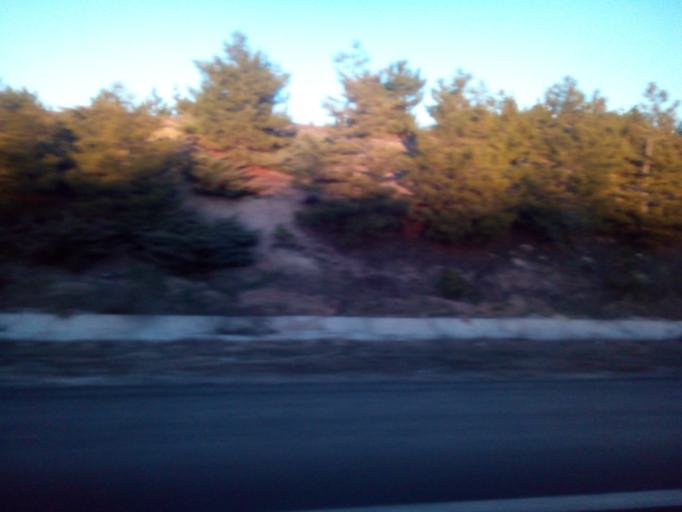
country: TR
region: Ankara
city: Etimesgut
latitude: 40.0174
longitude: 32.6254
